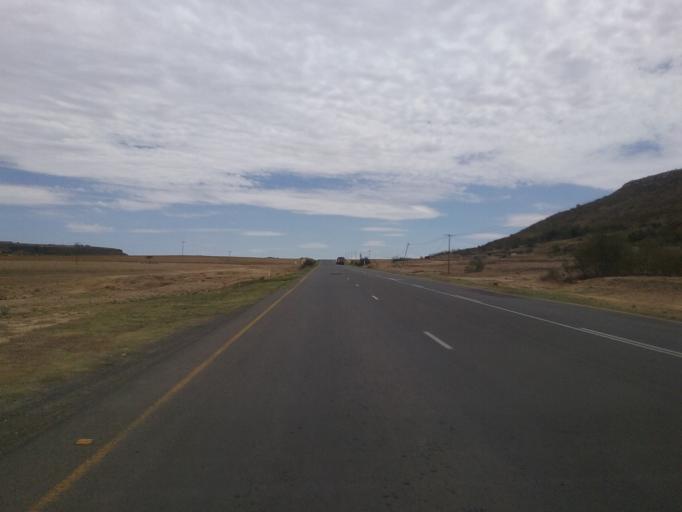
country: LS
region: Maseru
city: Nako
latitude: -29.6061
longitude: 27.5010
